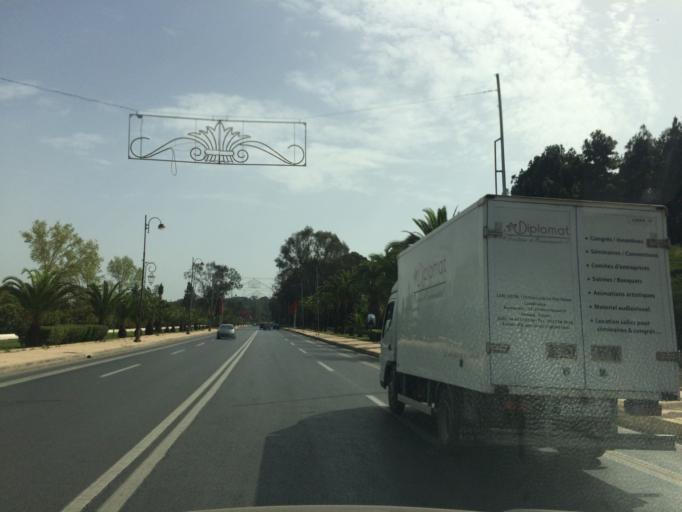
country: MA
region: Rabat-Sale-Zemmour-Zaer
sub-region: Rabat
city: Rabat
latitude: 33.9988
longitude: -6.8357
